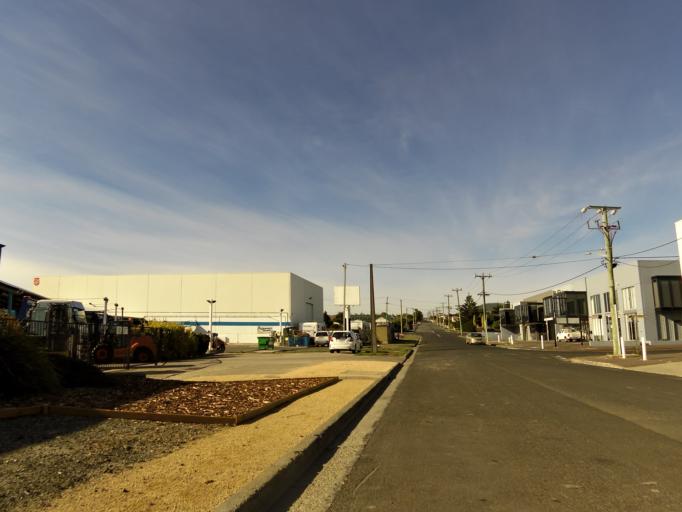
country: AU
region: Tasmania
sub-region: Glenorchy
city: Moonah
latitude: -42.8373
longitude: 147.3019
